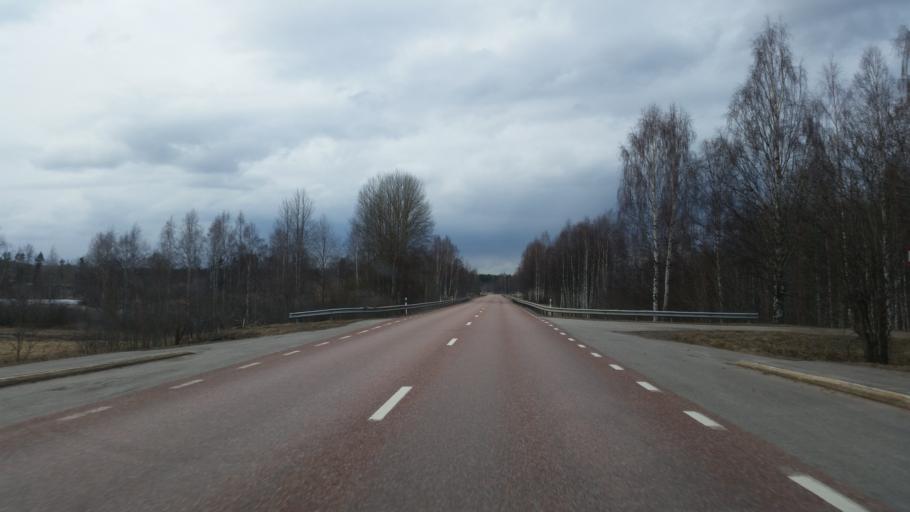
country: SE
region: Gaevleborg
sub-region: Ljusdals Kommun
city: Jaervsoe
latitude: 61.7571
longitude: 16.1608
